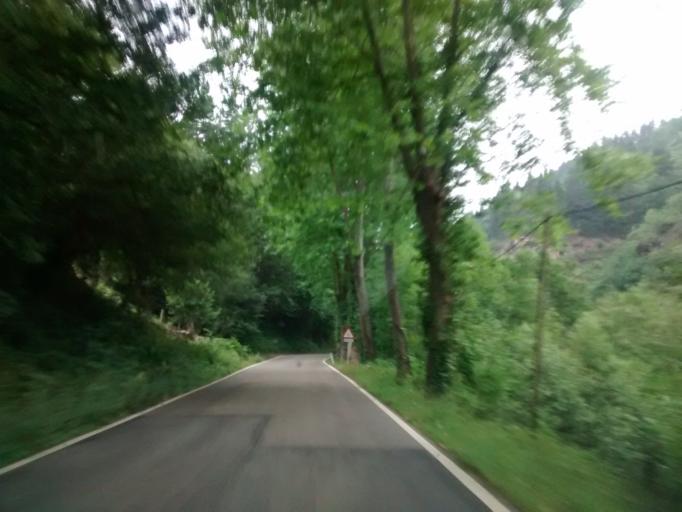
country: ES
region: Cantabria
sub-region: Provincia de Cantabria
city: Vega de Pas
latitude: 43.1624
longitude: -3.8247
